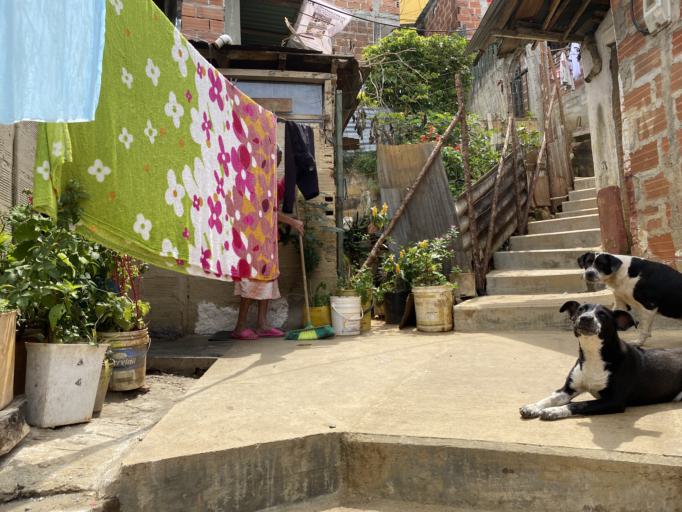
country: CO
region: Antioquia
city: Medellin
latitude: 6.2643
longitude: -75.5411
